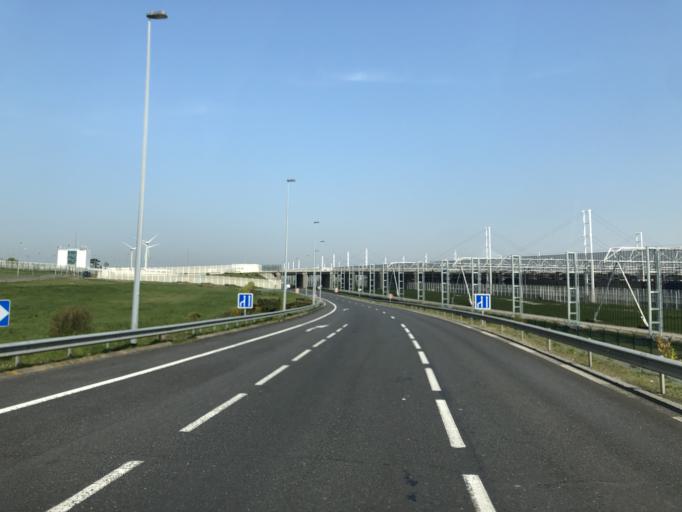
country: FR
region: Nord-Pas-de-Calais
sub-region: Departement du Pas-de-Calais
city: Frethun
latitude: 50.9202
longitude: 1.8090
